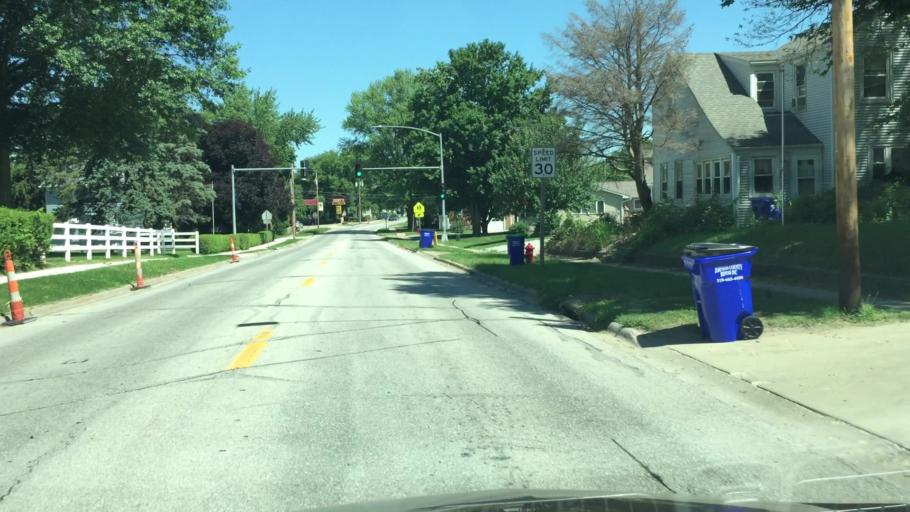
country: US
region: Iowa
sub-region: Johnson County
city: Solon
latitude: 41.8045
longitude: -91.4925
